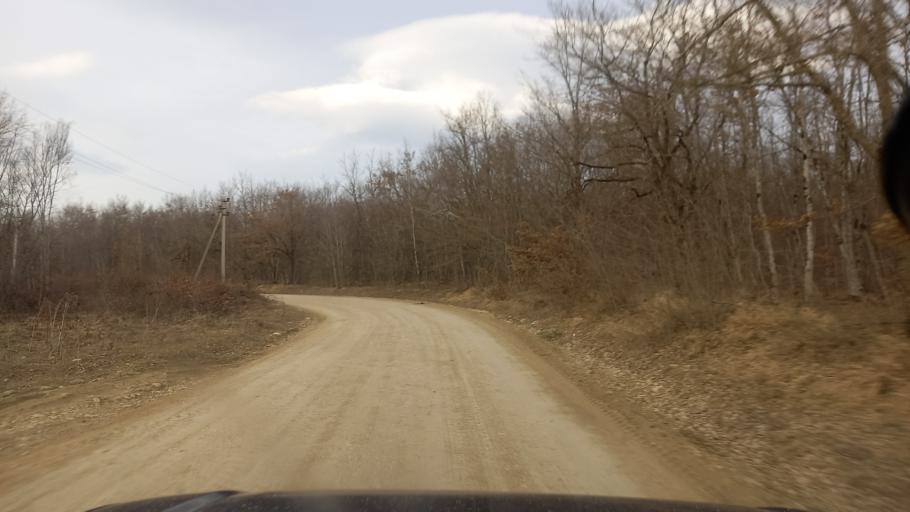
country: RU
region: Adygeya
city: Kamennomostskiy
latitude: 44.1439
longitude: 40.2580
